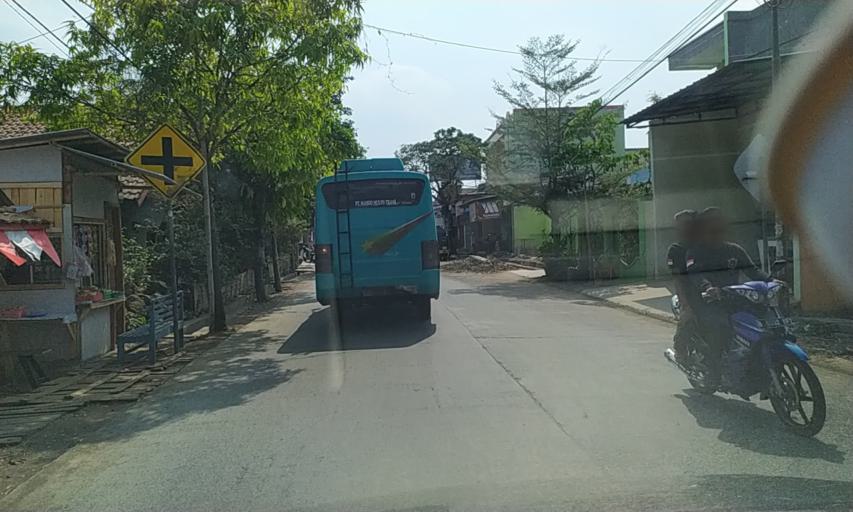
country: ID
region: Central Java
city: Tanjungsari
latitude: -7.3012
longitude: 108.7657
